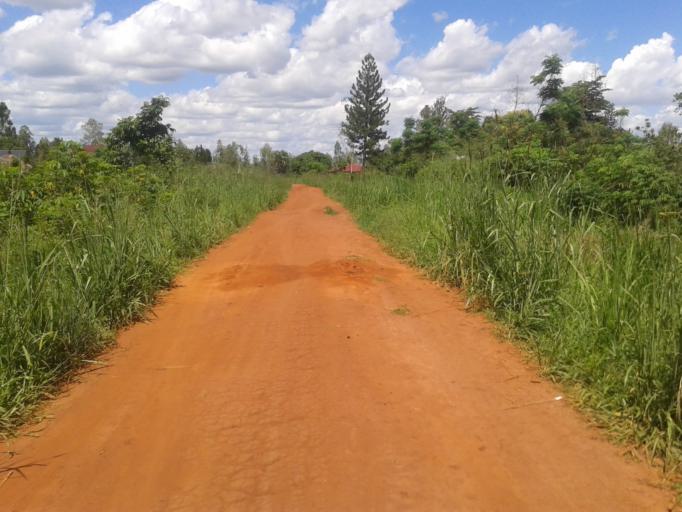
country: UG
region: Northern Region
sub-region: Gulu District
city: Gulu
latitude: 2.7586
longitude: 32.3250
